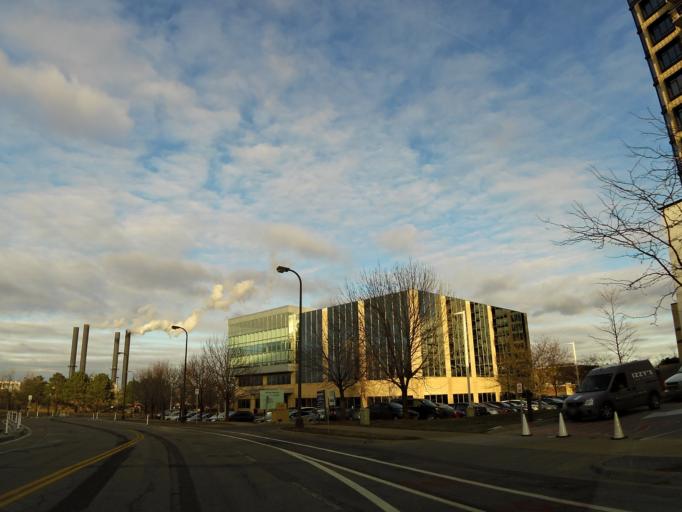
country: US
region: Minnesota
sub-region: Hennepin County
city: Minneapolis
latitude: 44.9766
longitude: -93.2521
